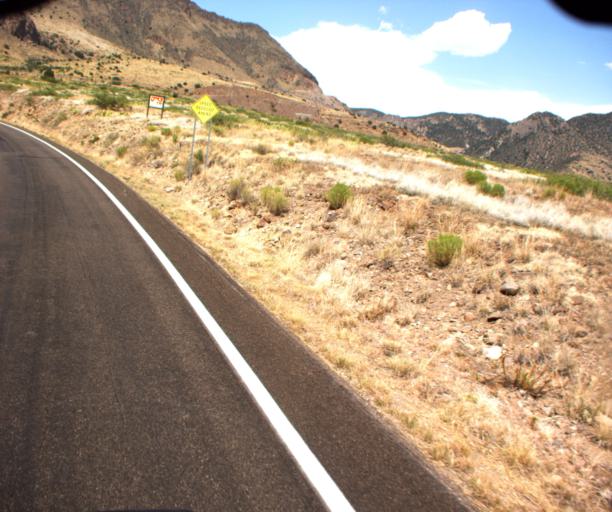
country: US
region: Arizona
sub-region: Greenlee County
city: Clifton
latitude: 33.0445
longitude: -109.1140
